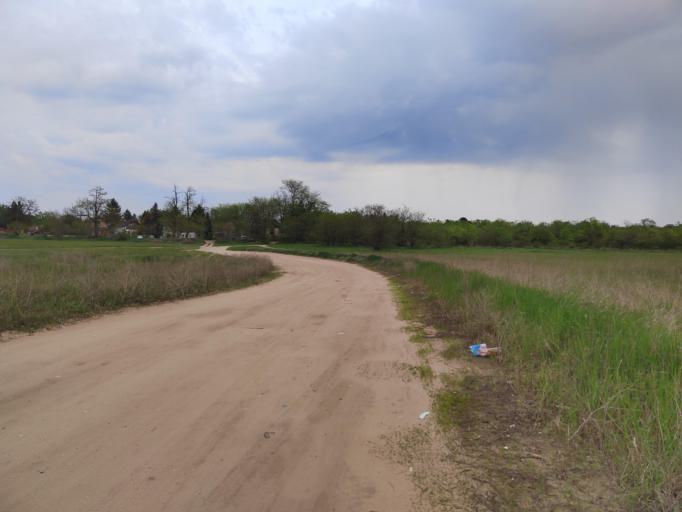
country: HU
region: Pest
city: Fot
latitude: 47.5906
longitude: 19.1905
